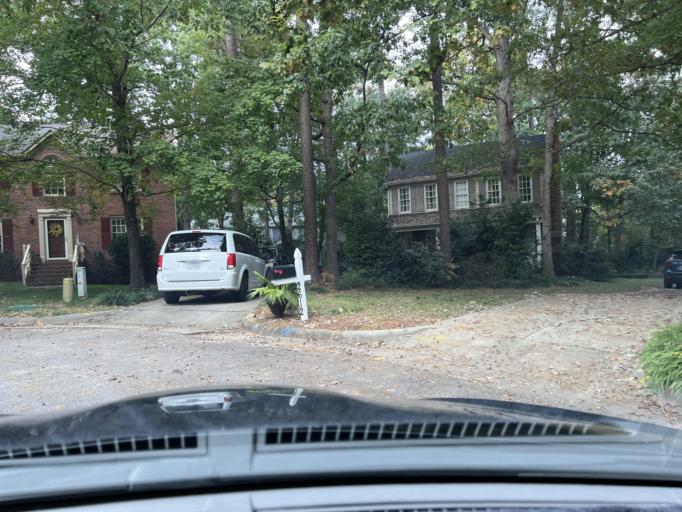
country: US
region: North Carolina
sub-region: Wake County
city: Wake Forest
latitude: 35.8990
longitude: -78.5942
